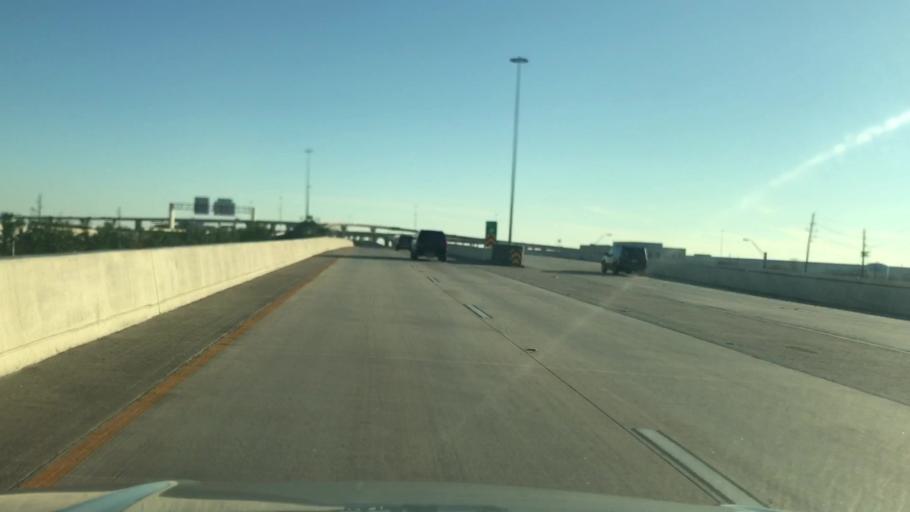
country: US
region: Texas
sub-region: Harris County
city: Katy
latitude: 29.7948
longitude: -95.7765
